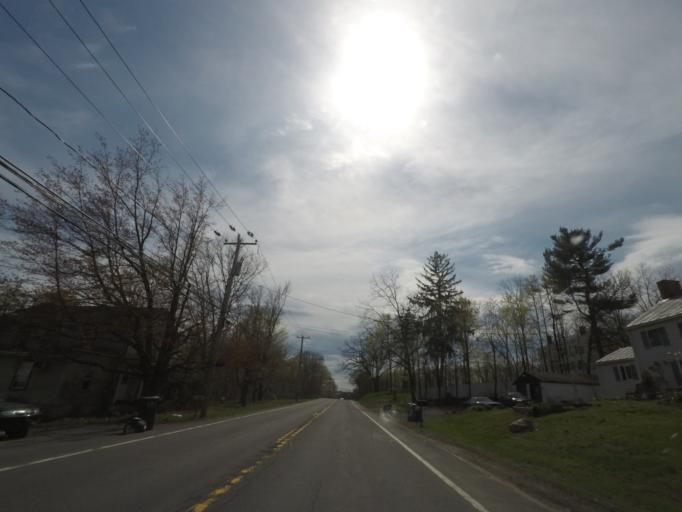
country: US
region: New York
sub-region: Columbia County
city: Chatham
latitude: 42.3185
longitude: -73.6295
